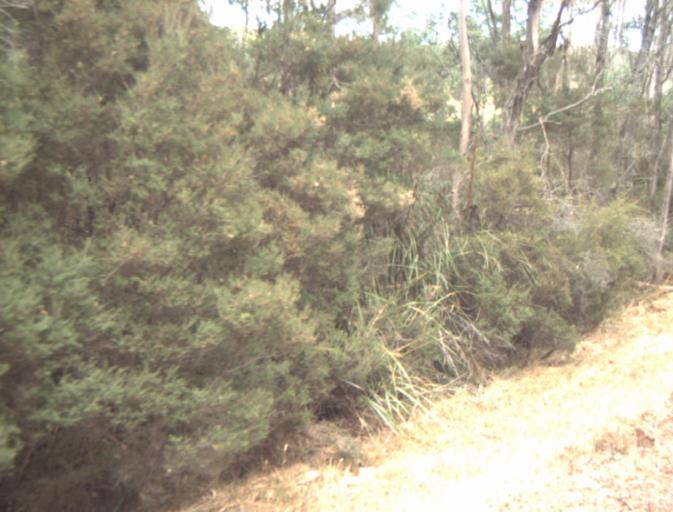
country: AU
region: Tasmania
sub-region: Launceston
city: Mayfield
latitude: -41.2157
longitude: 147.0527
